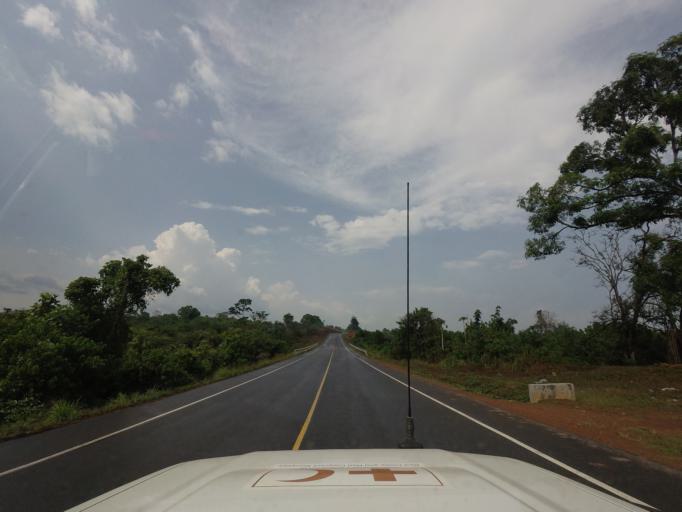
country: LR
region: Margibi
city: Kakata
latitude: 6.6243
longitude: -10.2547
